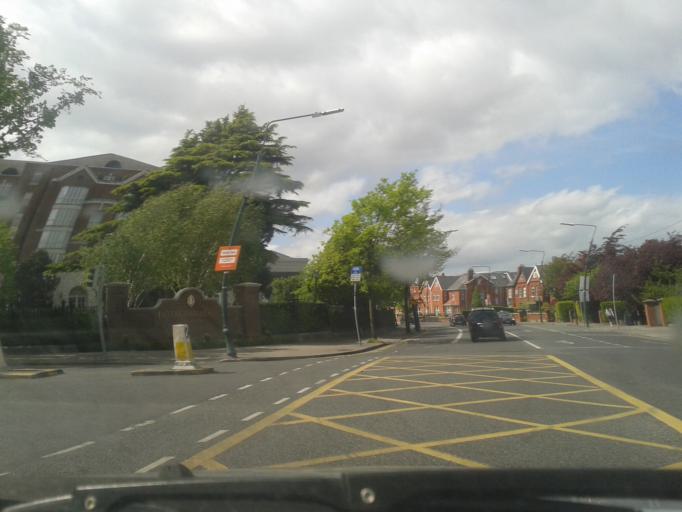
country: IE
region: Leinster
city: Donnybrook
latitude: 53.3264
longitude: -6.2244
